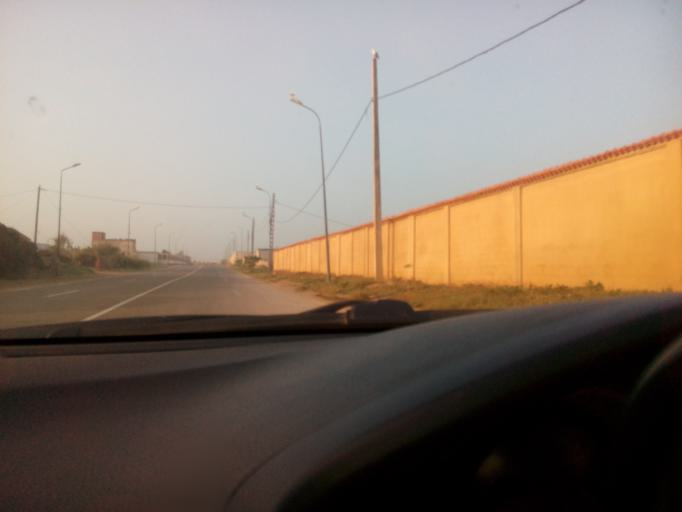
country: DZ
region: Oran
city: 'Ain el Turk
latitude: 35.7235
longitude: -0.8481
